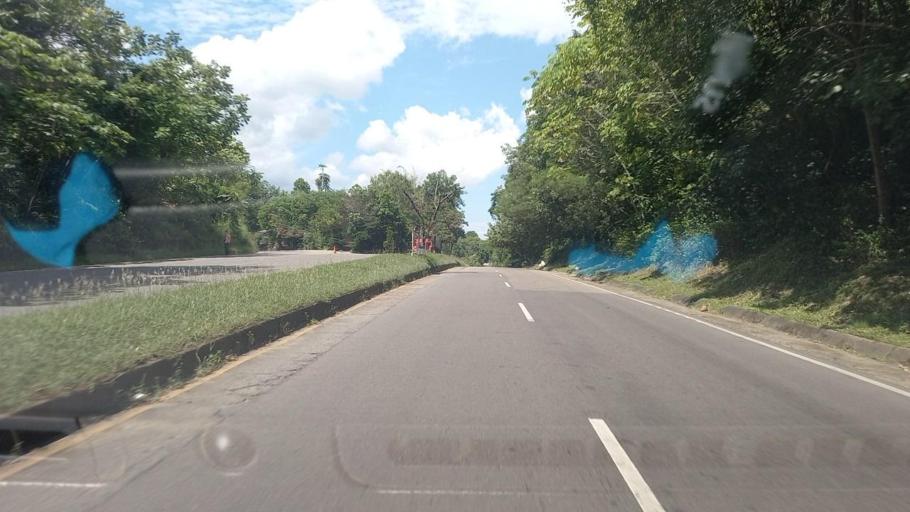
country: CO
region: Santander
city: Barrancabermeja
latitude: 7.1197
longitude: -73.6120
